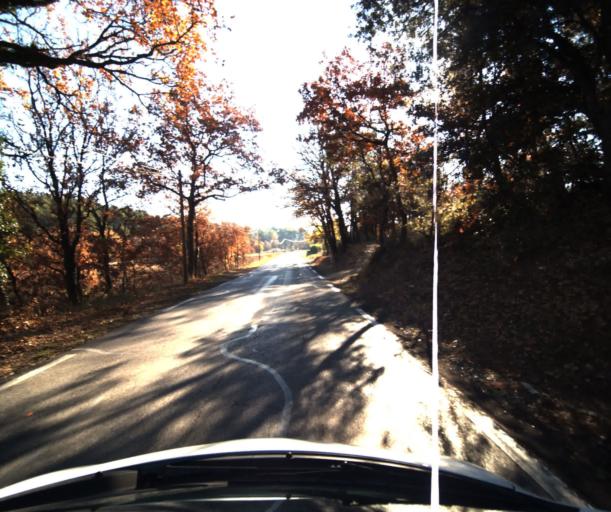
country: FR
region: Provence-Alpes-Cote d'Azur
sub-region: Departement du Vaucluse
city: Pertuis
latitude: 43.7183
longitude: 5.5048
